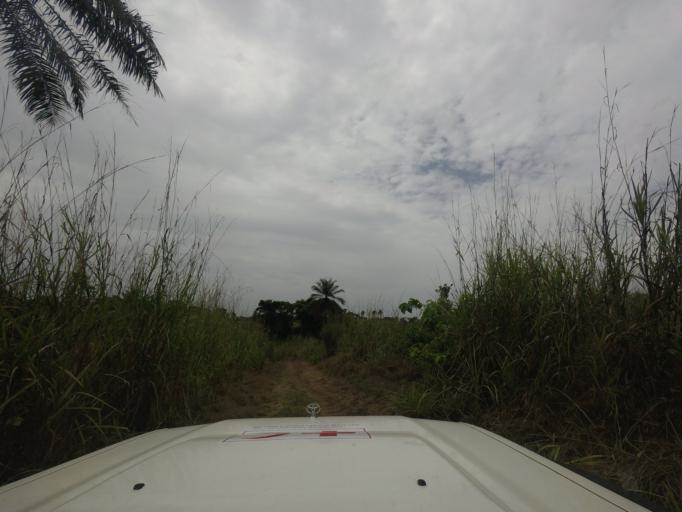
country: SL
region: Eastern Province
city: Buedu
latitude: 8.4268
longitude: -10.2631
